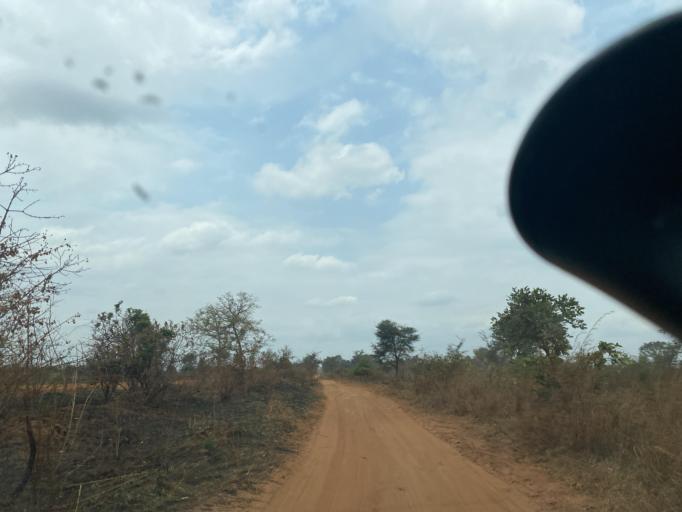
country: ZM
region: Lusaka
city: Chongwe
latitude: -15.4983
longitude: 28.8036
